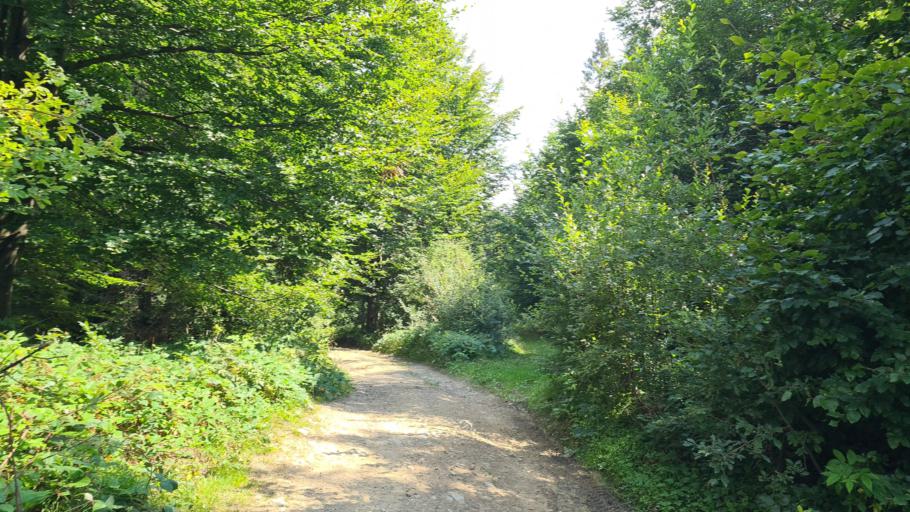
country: PL
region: Lesser Poland Voivodeship
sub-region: Powiat nowosadecki
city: Rytro
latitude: 49.4092
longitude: 20.6299
